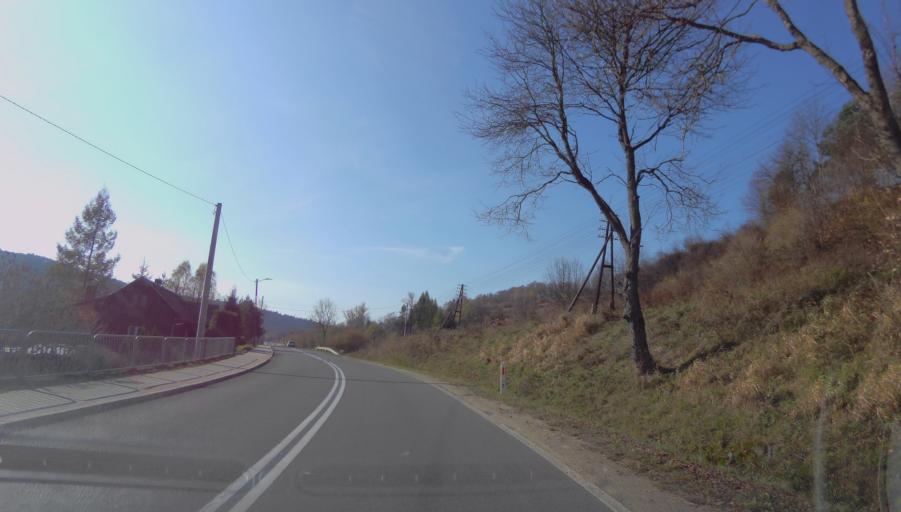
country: PL
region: Subcarpathian Voivodeship
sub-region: Powiat sanocki
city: Komancza
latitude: 49.3431
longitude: 22.0758
